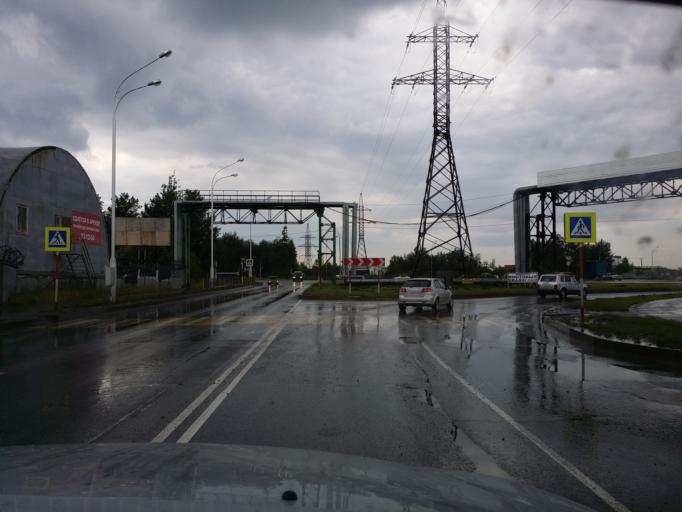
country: RU
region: Khanty-Mansiyskiy Avtonomnyy Okrug
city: Nizhnevartovsk
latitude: 60.9682
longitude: 76.5338
